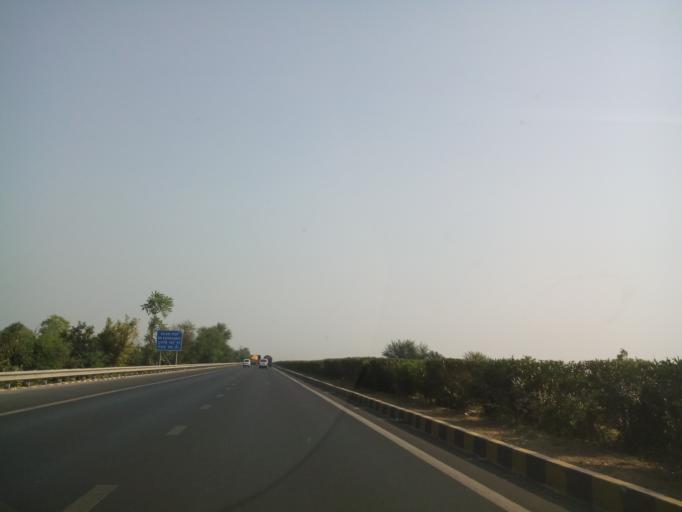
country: IN
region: Gujarat
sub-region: Ahmadabad
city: Ahmedabad
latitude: 22.9615
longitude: 72.6757
